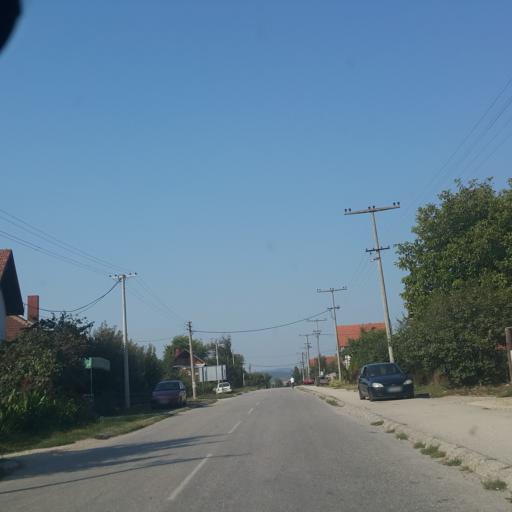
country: RS
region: Central Serbia
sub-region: Zajecarski Okrug
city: Zajecar
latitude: 43.9102
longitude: 22.2546
